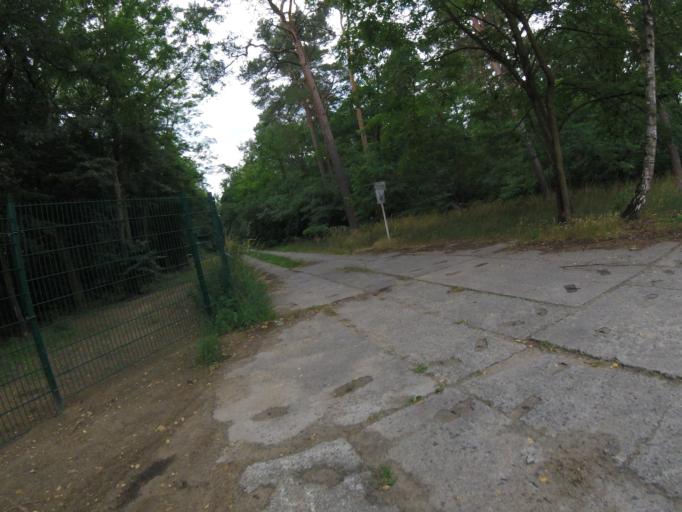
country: DE
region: Brandenburg
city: Konigs Wusterhausen
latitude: 52.2999
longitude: 13.6414
